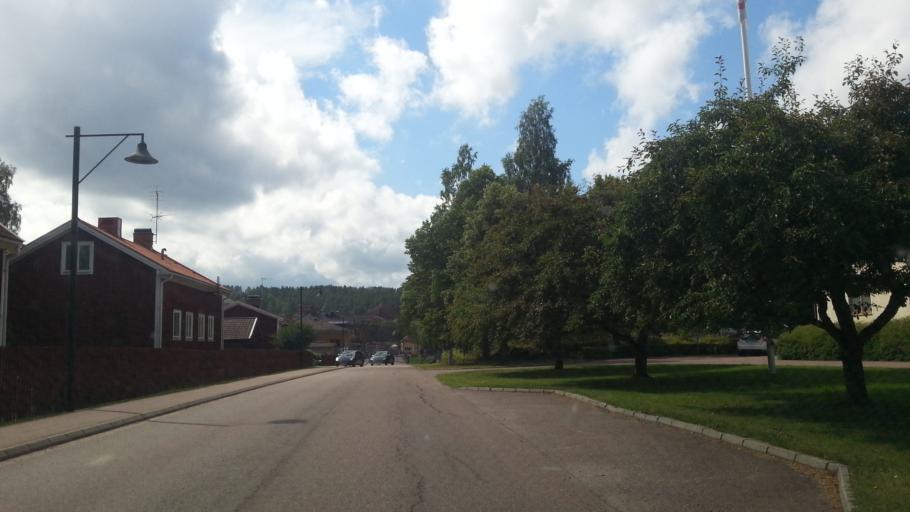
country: SE
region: Dalarna
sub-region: Faluns Kommun
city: Falun
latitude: 60.6015
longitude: 15.6191
